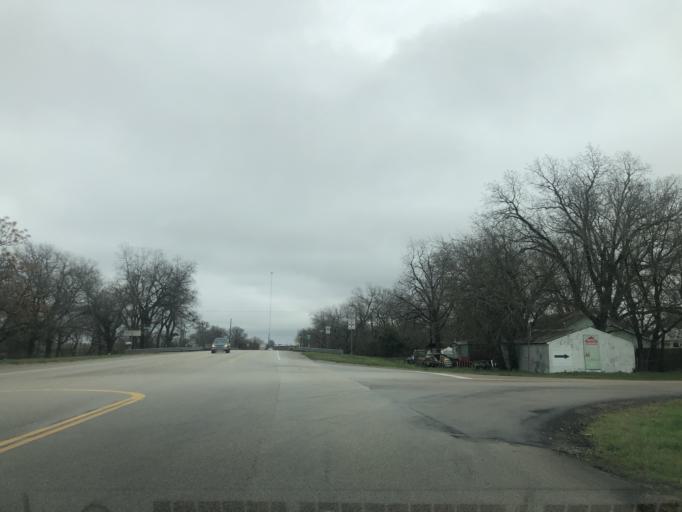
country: US
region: Texas
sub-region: Williamson County
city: Hutto
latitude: 30.6394
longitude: -97.5434
